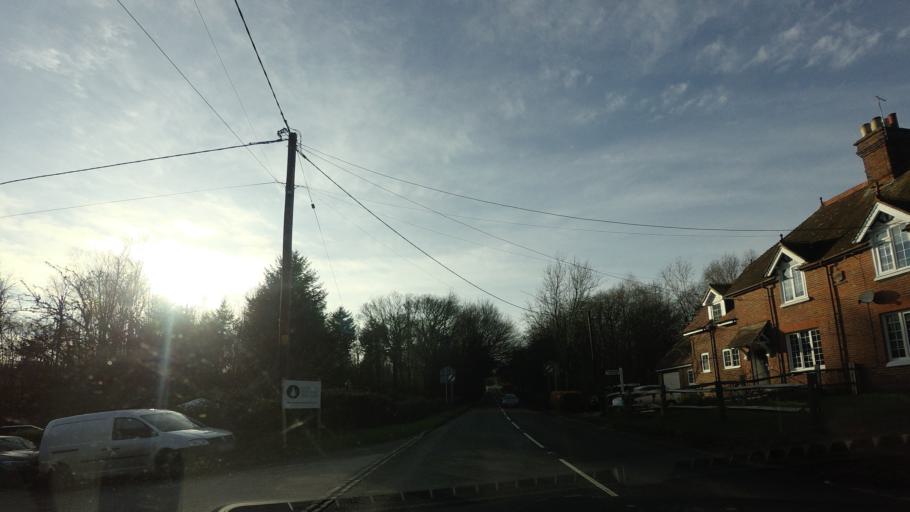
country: GB
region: England
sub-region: East Sussex
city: Bexhill-on-Sea
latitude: 50.8900
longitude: 0.4385
